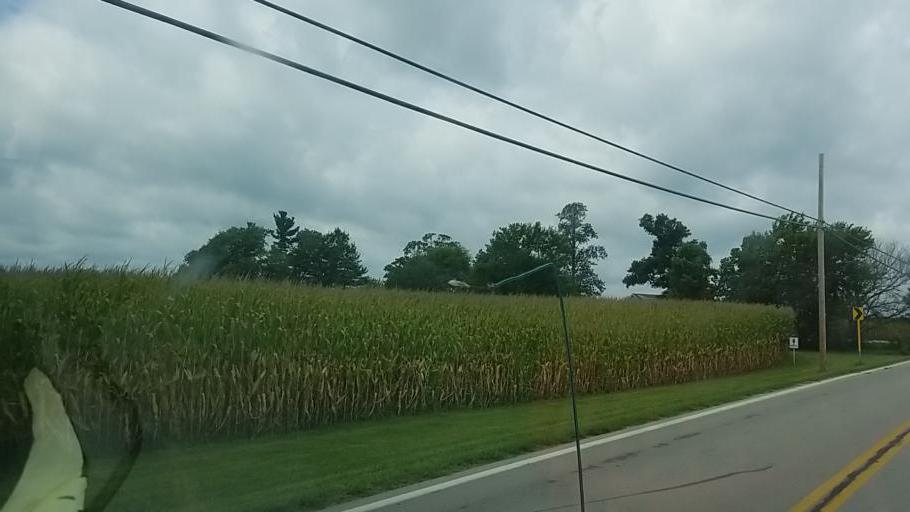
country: US
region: Ohio
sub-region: Madison County
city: Mount Sterling
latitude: 39.7532
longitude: -83.1901
